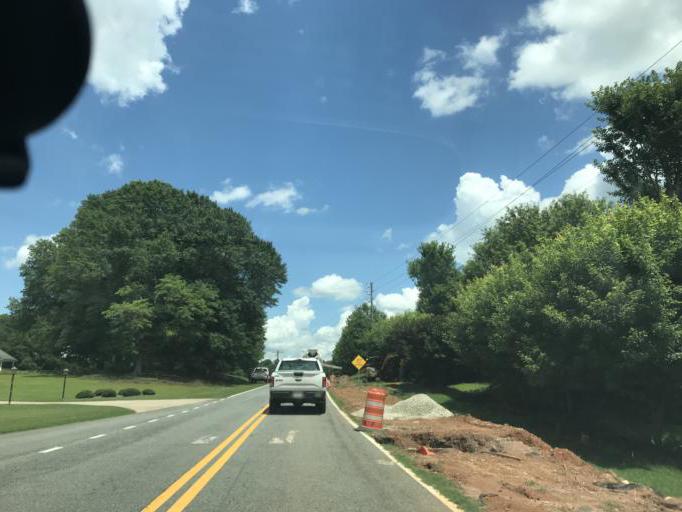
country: US
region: Georgia
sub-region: Forsyth County
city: Cumming
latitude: 34.1736
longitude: -84.1224
